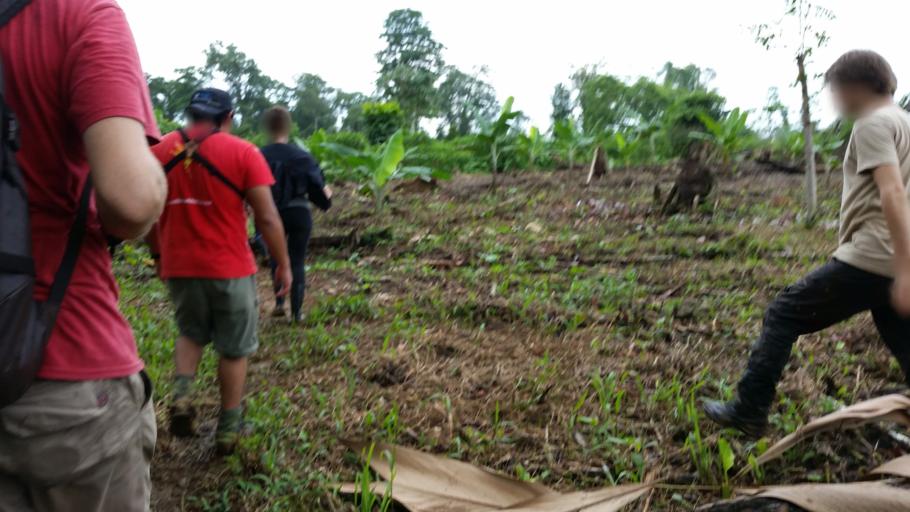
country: NI
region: Atlantico Norte (RAAN)
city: Bonanza
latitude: 14.0926
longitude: -84.6766
